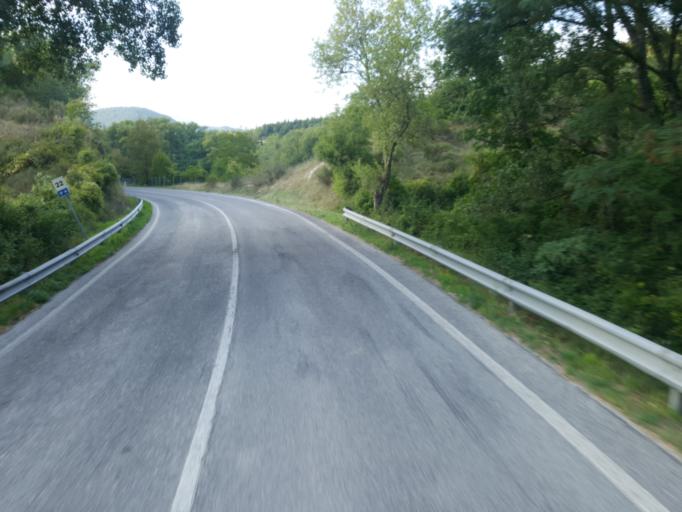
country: IT
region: The Marches
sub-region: Provincia di Ancona
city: Fabriano
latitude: 43.3353
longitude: 12.8330
